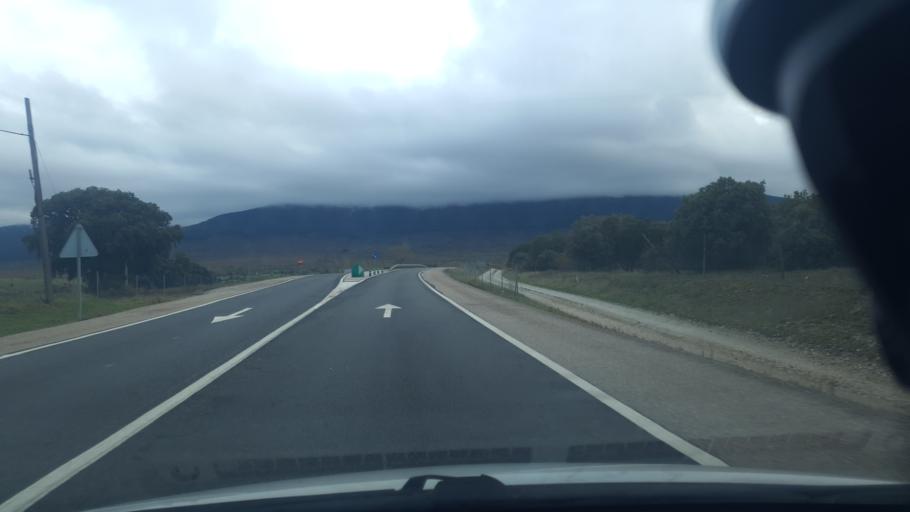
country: ES
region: Castille and Leon
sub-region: Provincia de Segovia
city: Cerezo de Abajo
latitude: 41.2113
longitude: -3.5831
